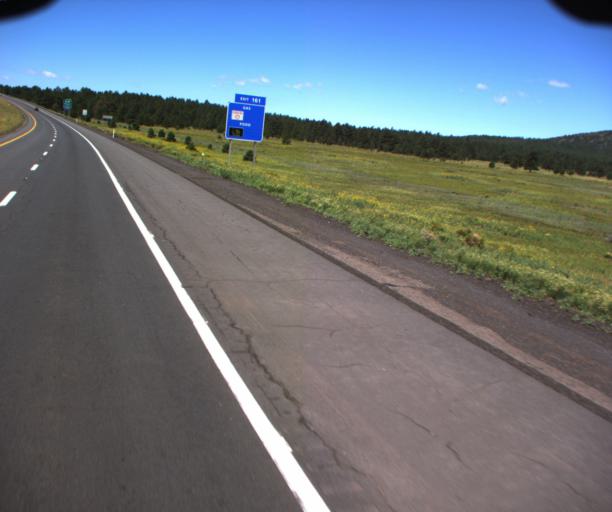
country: US
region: Arizona
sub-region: Coconino County
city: Williams
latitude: 35.2546
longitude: -112.2023
